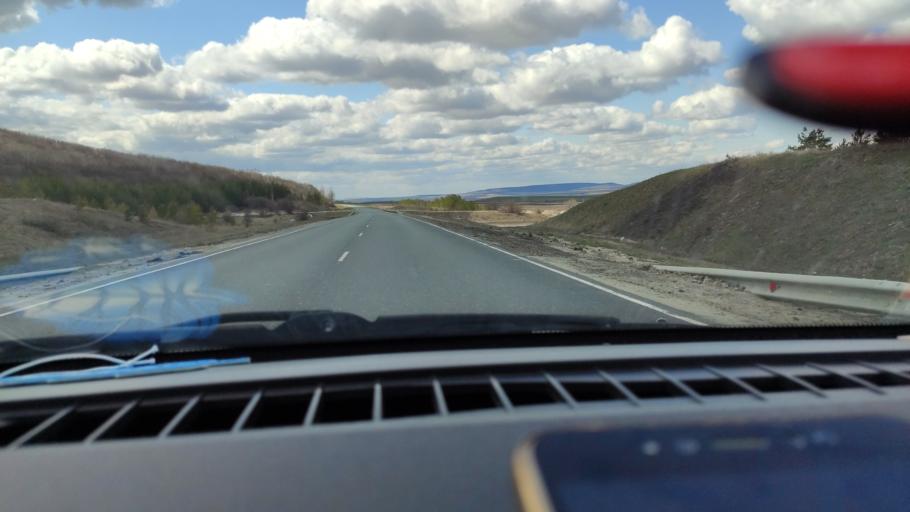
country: RU
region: Saratov
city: Alekseyevka
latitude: 52.3924
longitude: 47.9784
